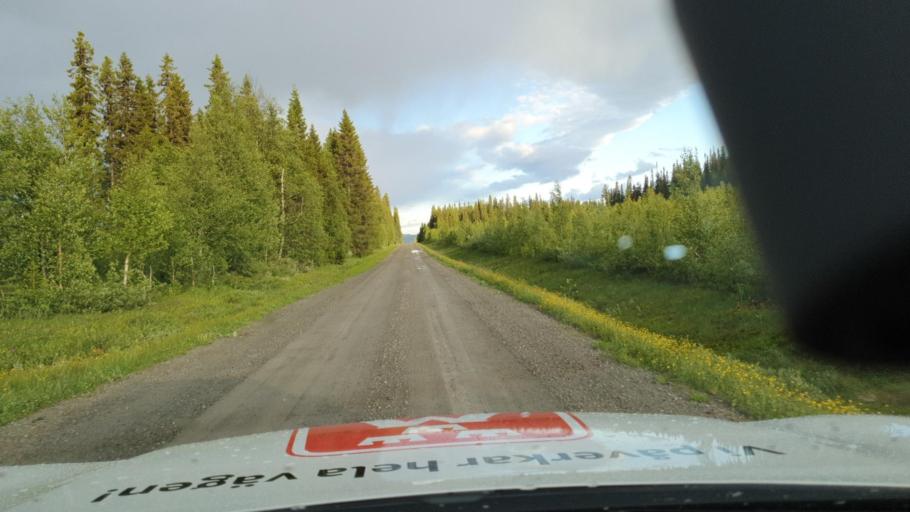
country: SE
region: Vaesterbotten
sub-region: Storumans Kommun
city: Storuman
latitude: 64.7709
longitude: 17.0456
